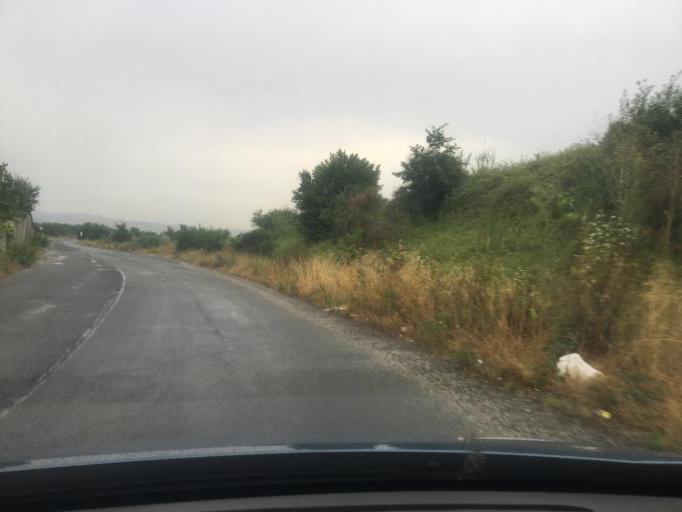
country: BG
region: Burgas
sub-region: Obshtina Burgas
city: Burgas
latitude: 42.5530
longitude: 27.4918
